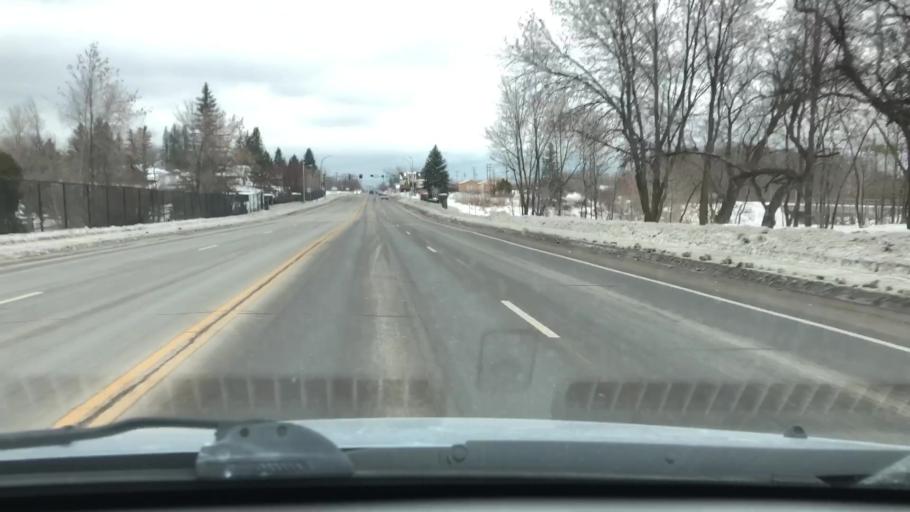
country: US
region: Minnesota
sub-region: Saint Louis County
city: Proctor
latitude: 46.7237
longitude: -92.1907
